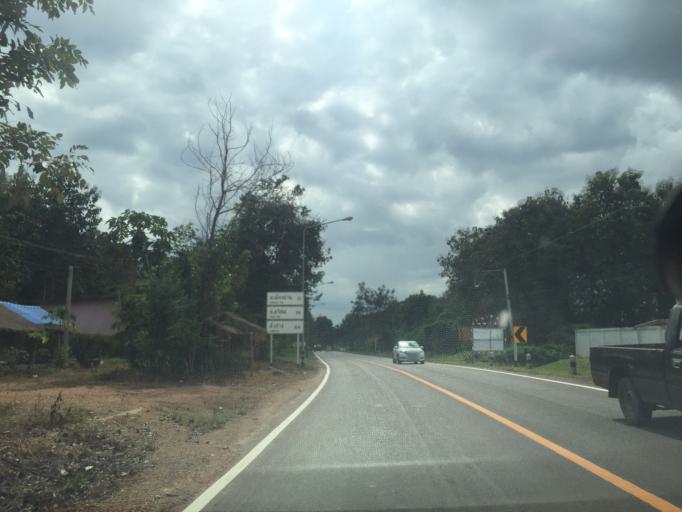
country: TH
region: Lampang
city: Mueang Pan
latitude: 18.8277
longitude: 99.4957
